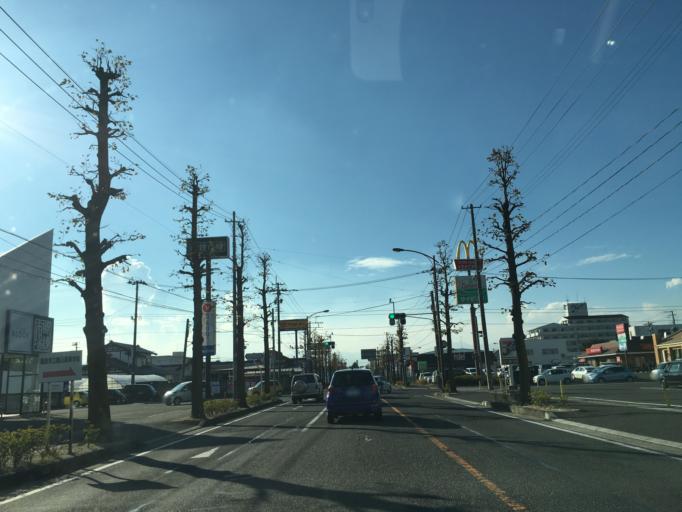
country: JP
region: Fukushima
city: Koriyama
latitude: 37.3989
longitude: 140.3348
